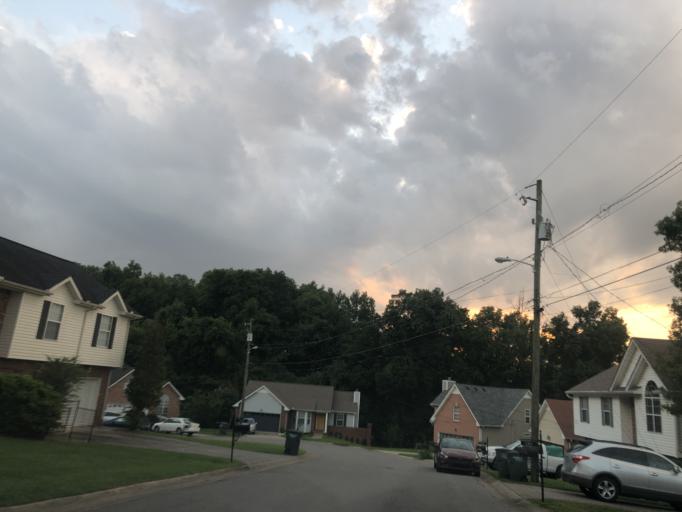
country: US
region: Tennessee
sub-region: Davidson County
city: Lakewood
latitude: 36.1467
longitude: -86.6385
